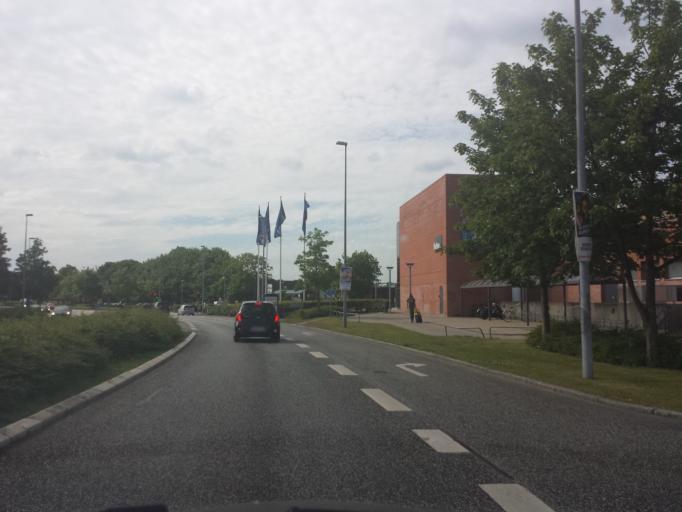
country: DK
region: Capital Region
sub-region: Ballerup Kommune
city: Ballerup
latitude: 55.7284
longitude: 12.3567
